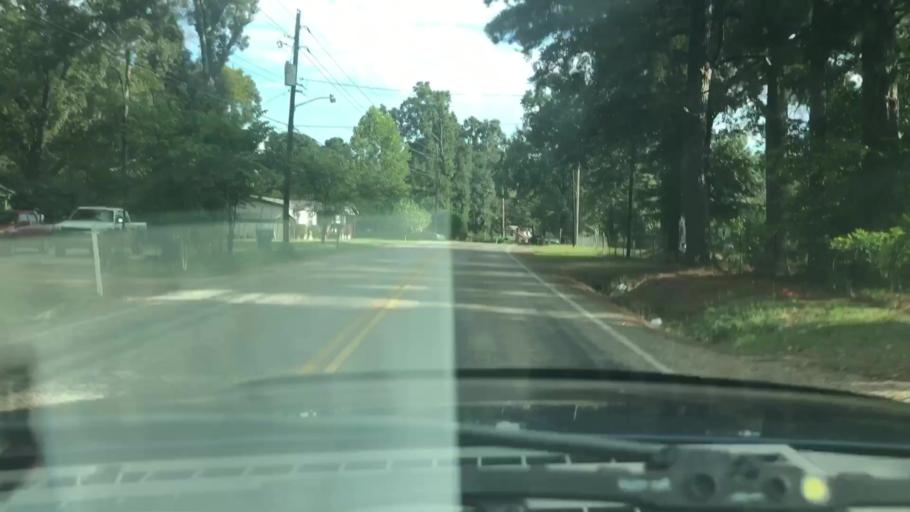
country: US
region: Texas
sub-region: Bowie County
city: Texarkana
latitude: 33.4009
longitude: -94.0643
